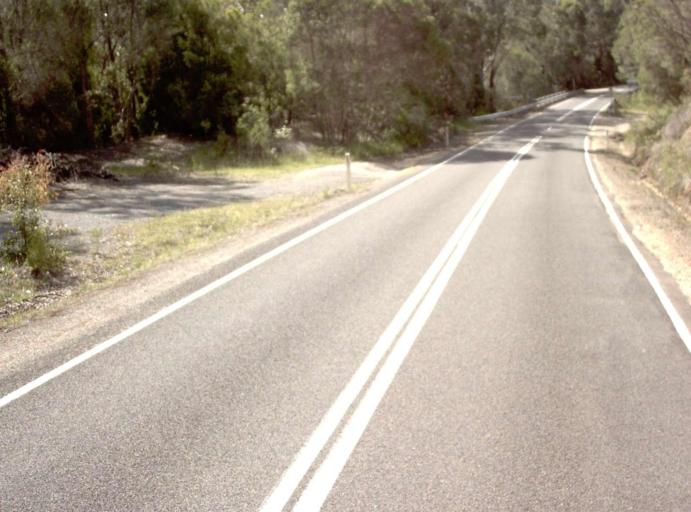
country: AU
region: New South Wales
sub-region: Bega Valley
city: Eden
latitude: -37.5309
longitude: 149.6898
